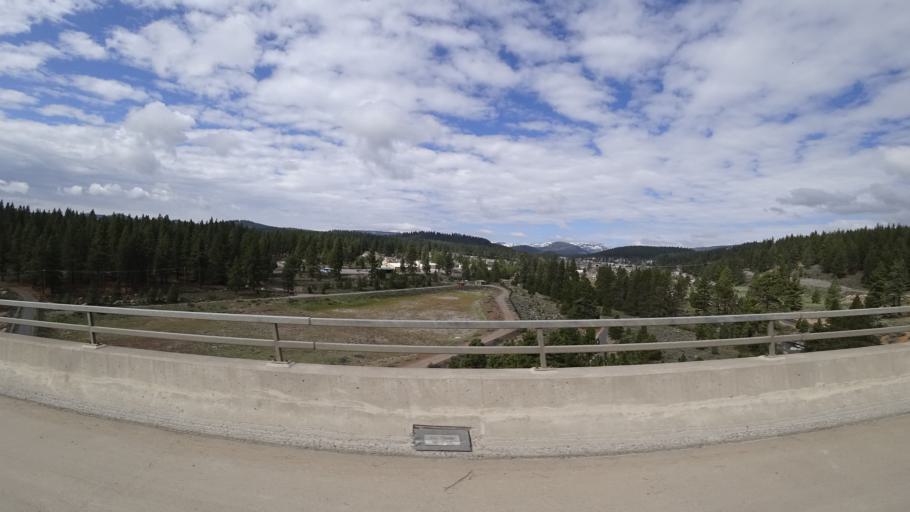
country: US
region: California
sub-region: Nevada County
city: Truckee
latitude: 39.3324
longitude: -120.1623
